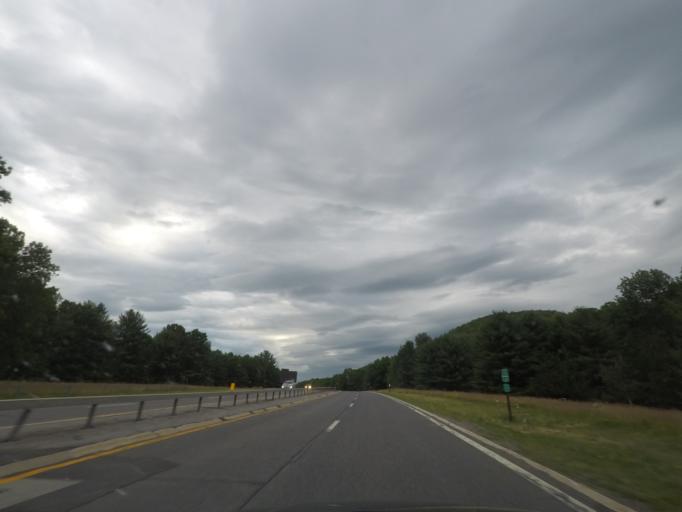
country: US
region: New York
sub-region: Dutchess County
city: Pine Plains
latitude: 42.0296
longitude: -73.7323
